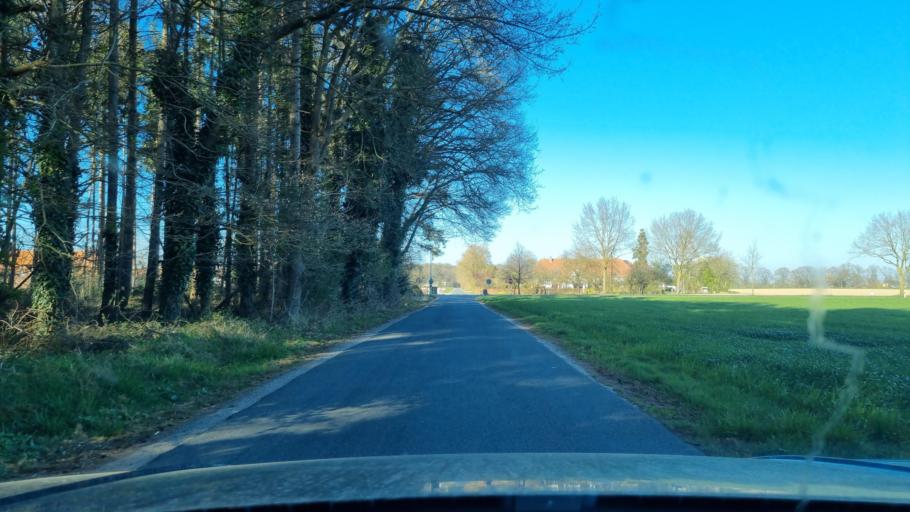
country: DE
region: North Rhine-Westphalia
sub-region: Regierungsbezirk Dusseldorf
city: Kleve
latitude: 51.7397
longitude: 6.1497
